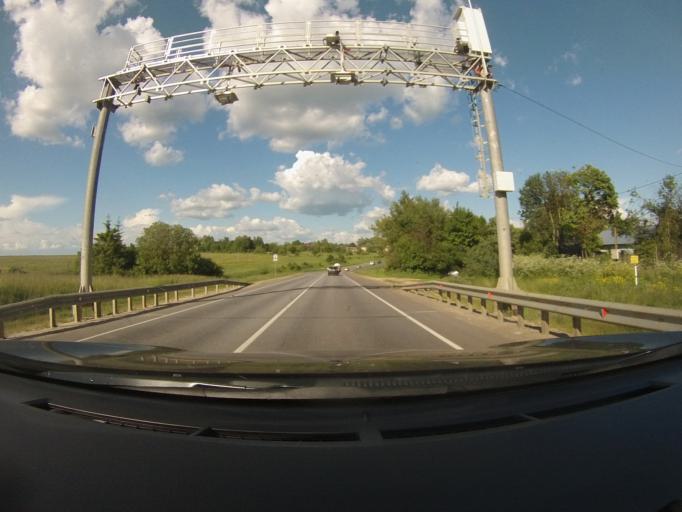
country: RU
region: Tula
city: Bol'shoye Skuratovo
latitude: 53.4539
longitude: 36.8642
